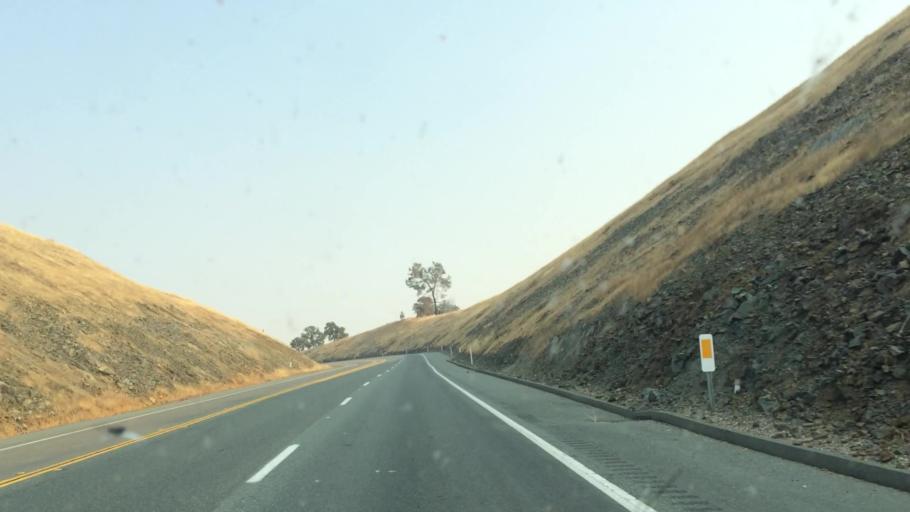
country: US
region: California
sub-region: Amador County
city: Sutter Creek
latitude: 38.4105
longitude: -120.8349
